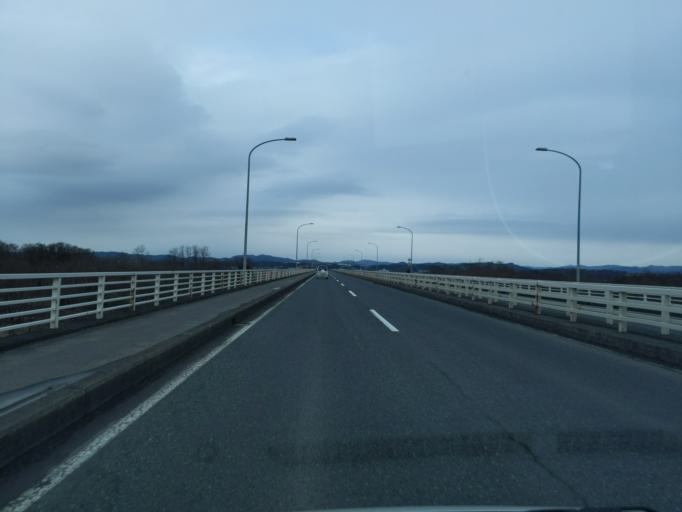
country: JP
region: Iwate
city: Mizusawa
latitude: 39.1677
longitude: 141.1555
